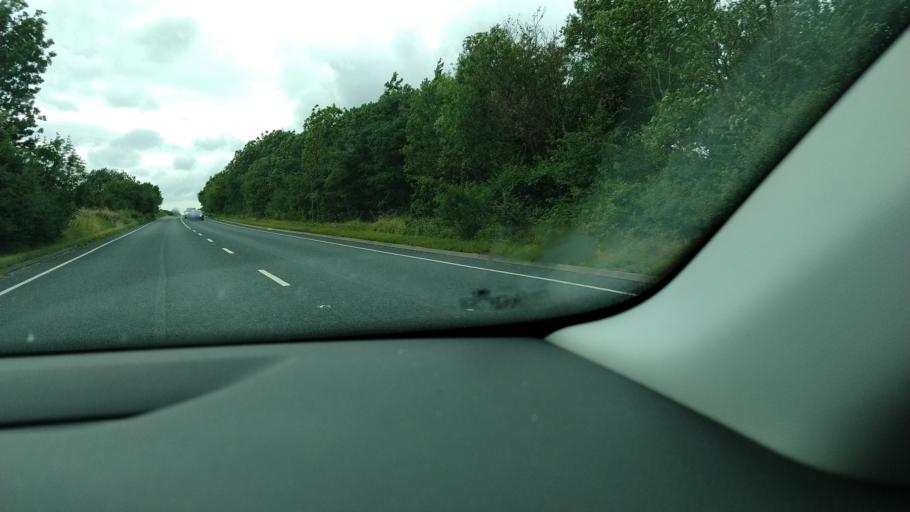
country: GB
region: England
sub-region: East Riding of Yorkshire
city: Rawcliffe
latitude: 53.7131
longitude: -0.9547
